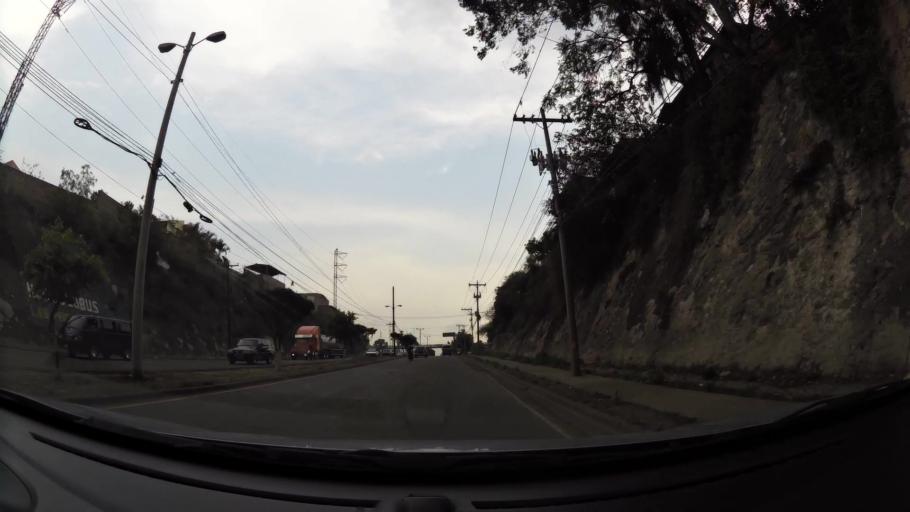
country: HN
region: Francisco Morazan
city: Tegucigalpa
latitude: 14.0940
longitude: -87.2392
